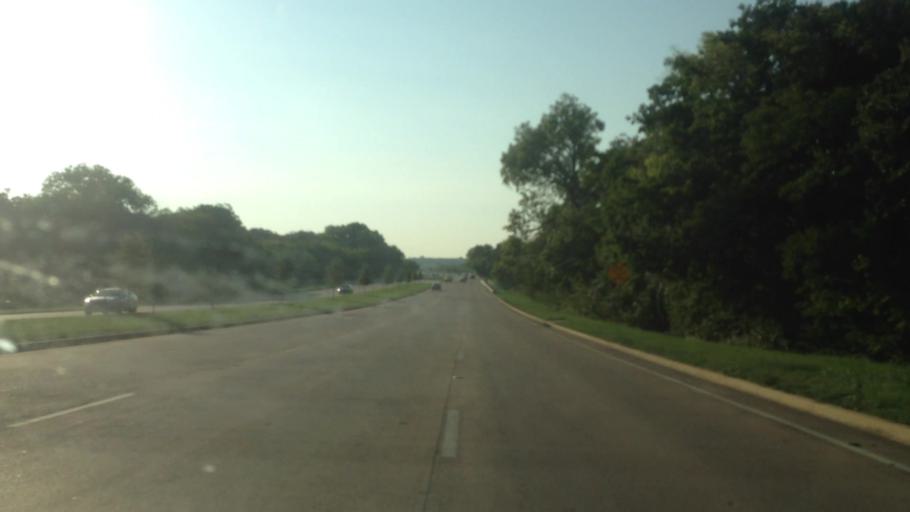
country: US
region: Texas
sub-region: Tarrant County
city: Pantego
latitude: 32.7169
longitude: -97.1704
